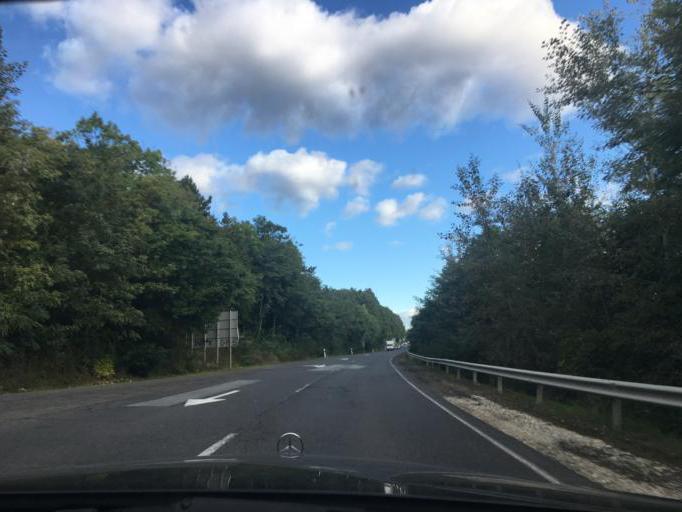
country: HU
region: Borsod-Abauj-Zemplen
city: Gonc
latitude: 48.4307
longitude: 21.1818
